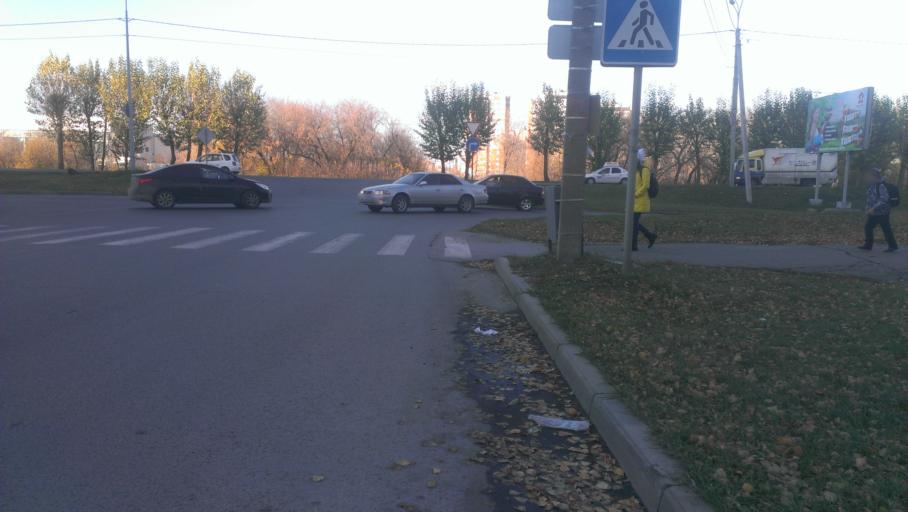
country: RU
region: Altai Krai
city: Novosilikatnyy
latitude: 53.3447
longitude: 83.6628
